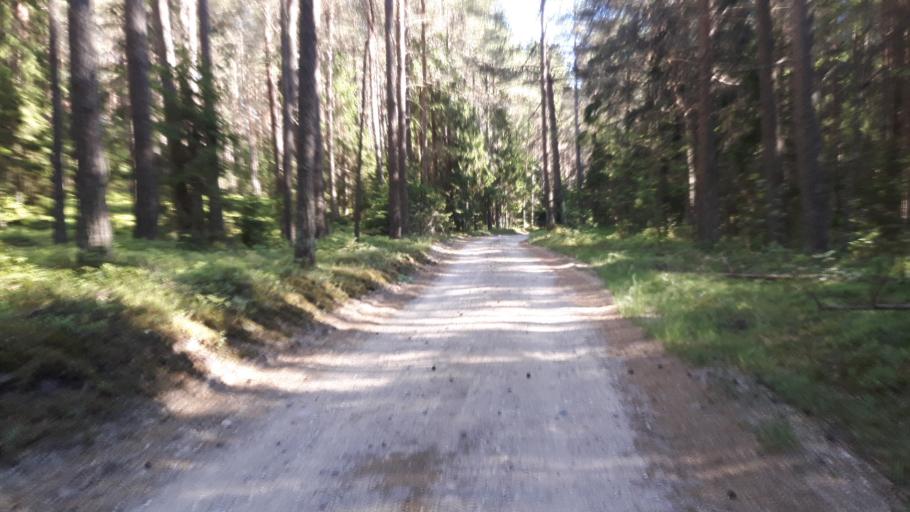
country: LV
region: Salacgrivas
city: Salacgriva
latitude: 57.7288
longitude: 24.3497
